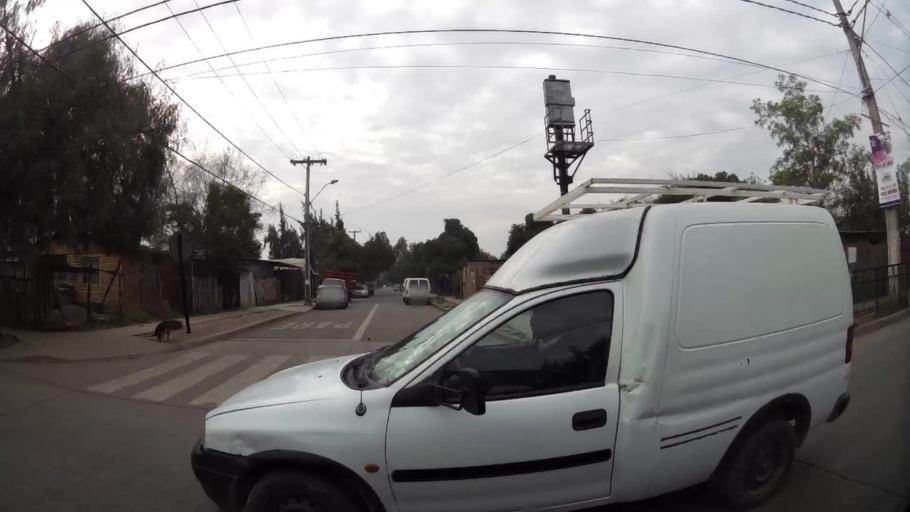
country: CL
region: Santiago Metropolitan
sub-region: Provincia de Chacabuco
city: Lampa
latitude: -33.2294
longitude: -70.8078
